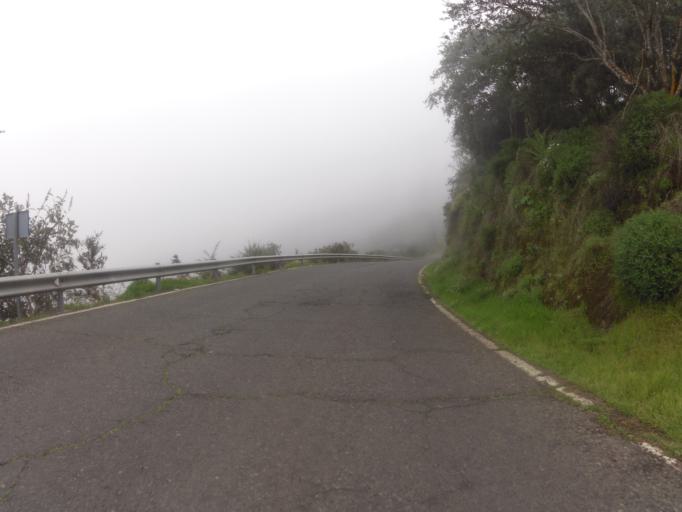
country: ES
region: Canary Islands
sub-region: Provincia de Las Palmas
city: Tejeda
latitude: 27.9844
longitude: -15.5725
